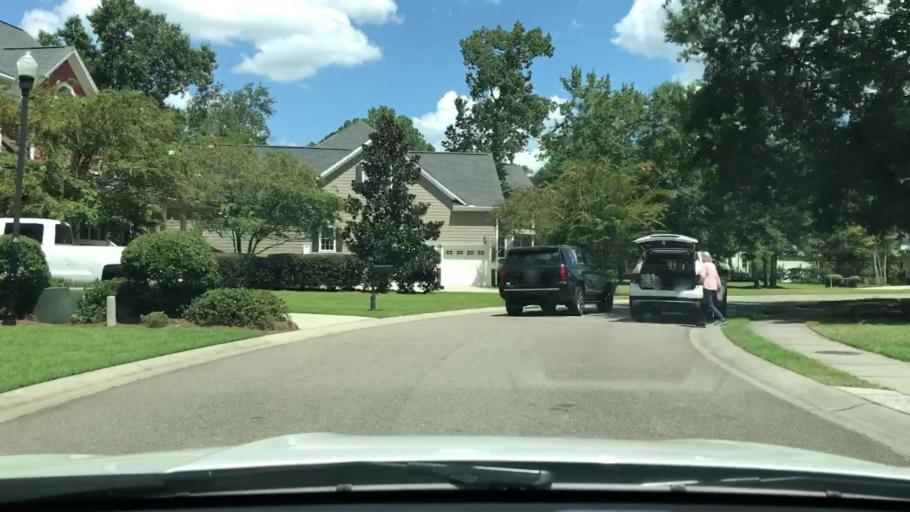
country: US
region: South Carolina
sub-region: Berkeley County
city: Hanahan
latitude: 32.9282
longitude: -79.9999
